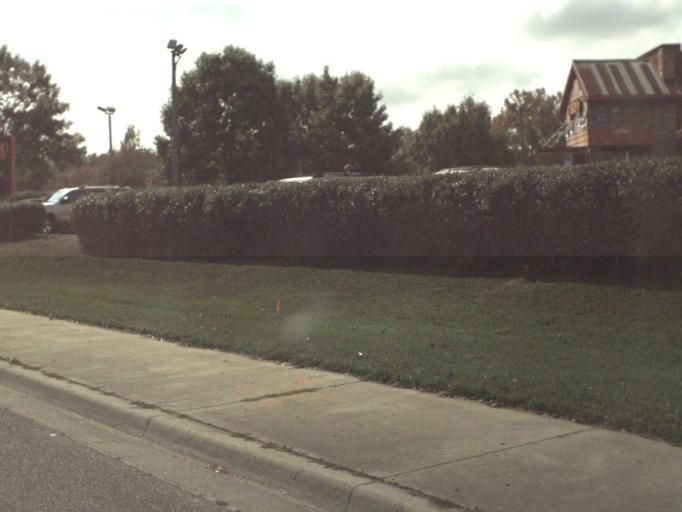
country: US
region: Florida
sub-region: Leon County
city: Tallahassee
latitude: 30.4767
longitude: -84.2363
